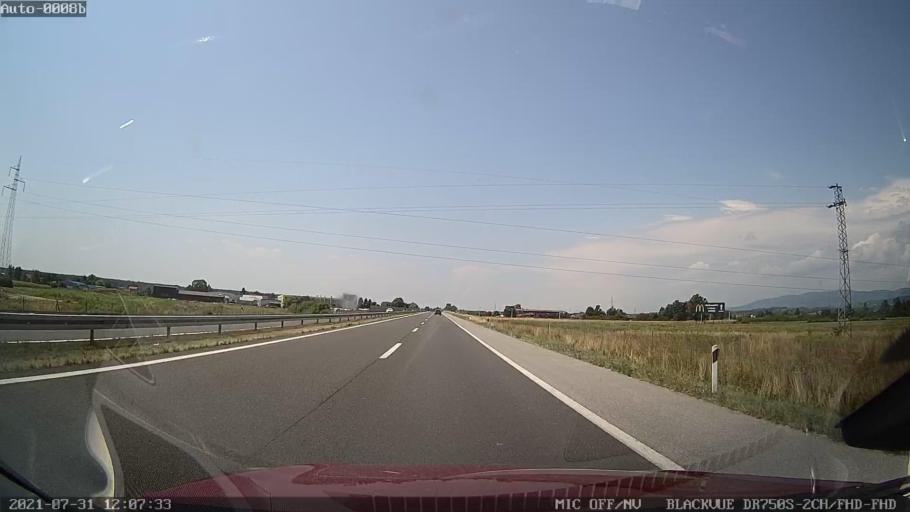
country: HR
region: Grad Zagreb
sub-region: Sesvete
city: Sesvete
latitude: 45.8595
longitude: 16.1663
